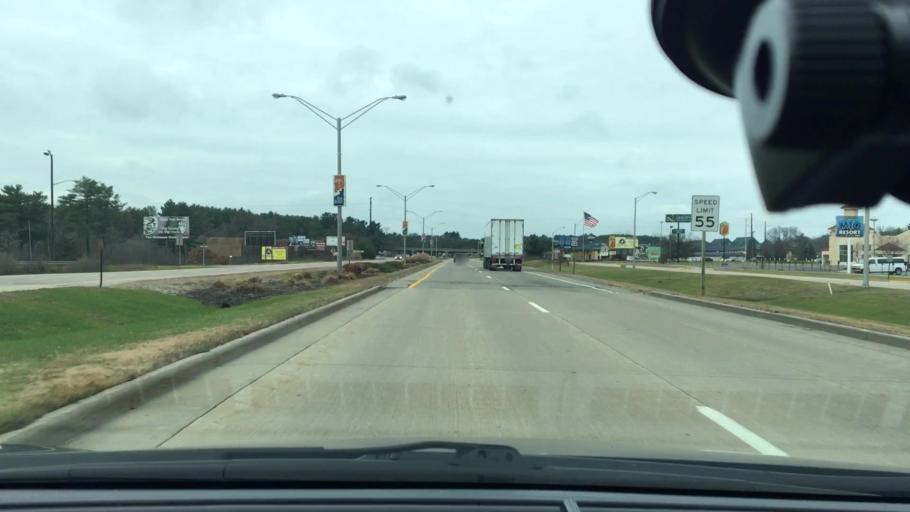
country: US
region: Wisconsin
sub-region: Sauk County
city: Lake Delton
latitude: 43.6243
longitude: -89.7951
